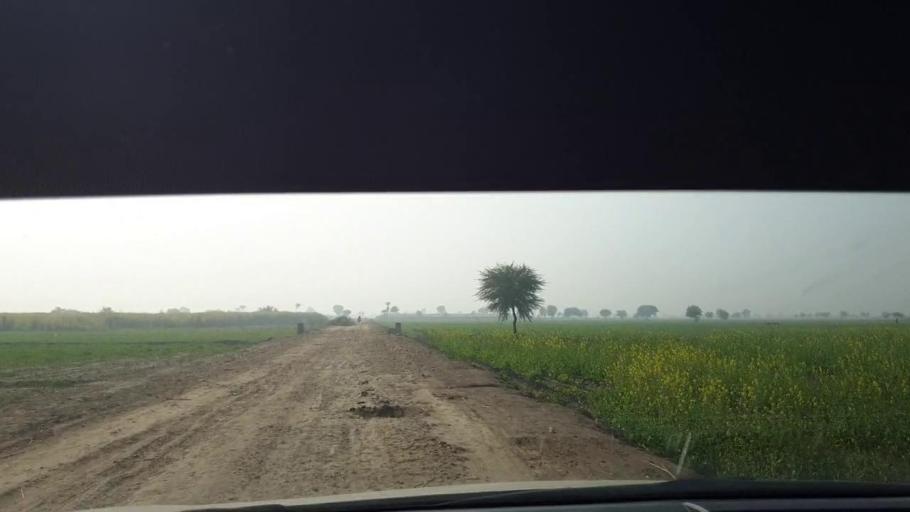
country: PK
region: Sindh
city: Berani
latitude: 25.7842
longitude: 68.7977
